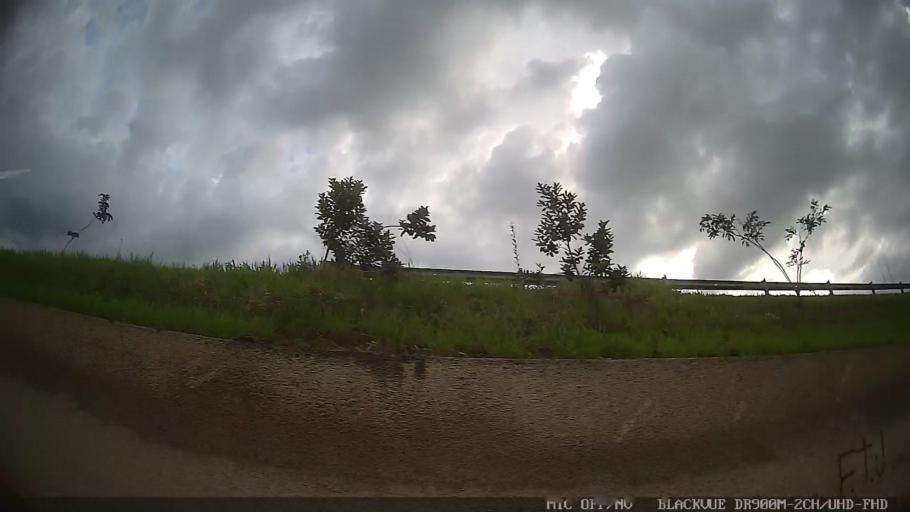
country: BR
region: Sao Paulo
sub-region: Jaguariuna
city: Jaguariuna
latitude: -22.6958
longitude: -47.0106
